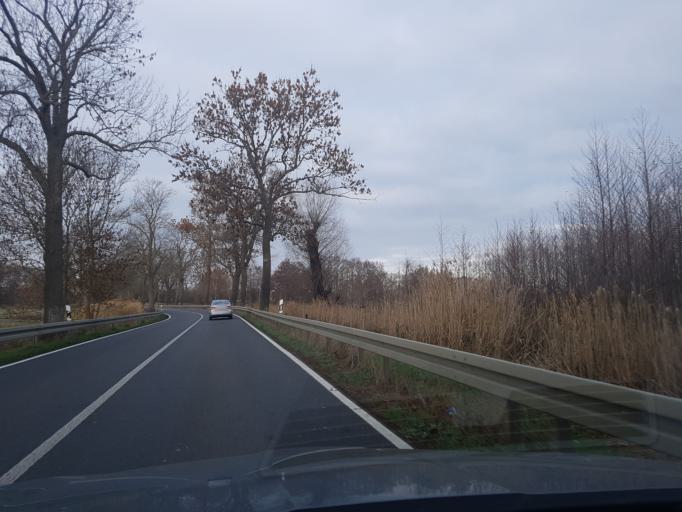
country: DE
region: Brandenburg
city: Golssen
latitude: 51.9623
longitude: 13.6222
